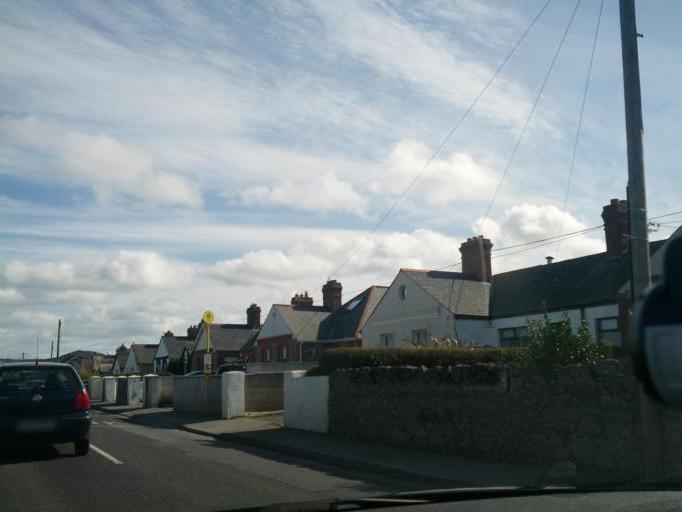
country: IE
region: Leinster
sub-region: Fingal County
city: Baldoyle
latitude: 53.3934
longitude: -6.1205
